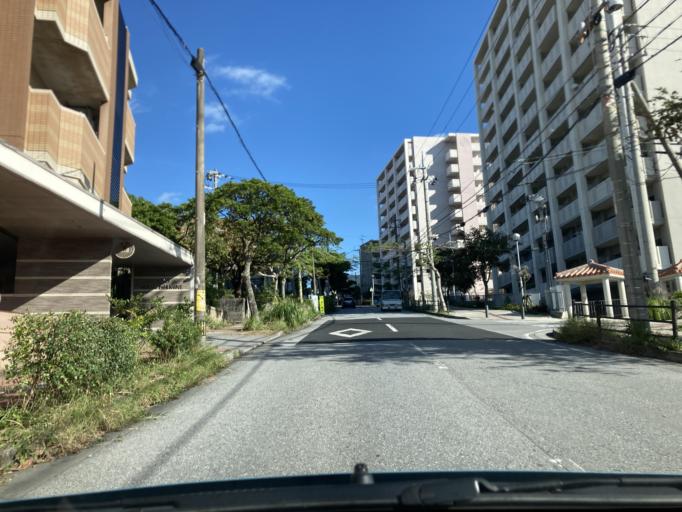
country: JP
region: Okinawa
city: Ginowan
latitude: 26.2251
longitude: 127.7321
